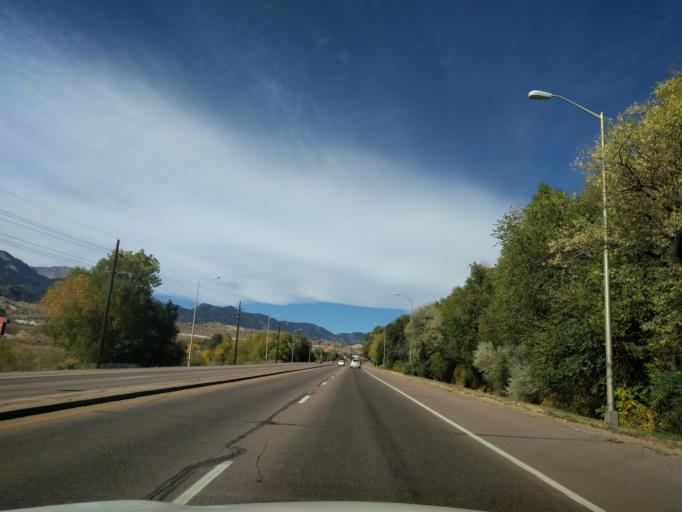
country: US
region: Colorado
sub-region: El Paso County
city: Colorado Springs
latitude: 38.8376
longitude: -104.8534
